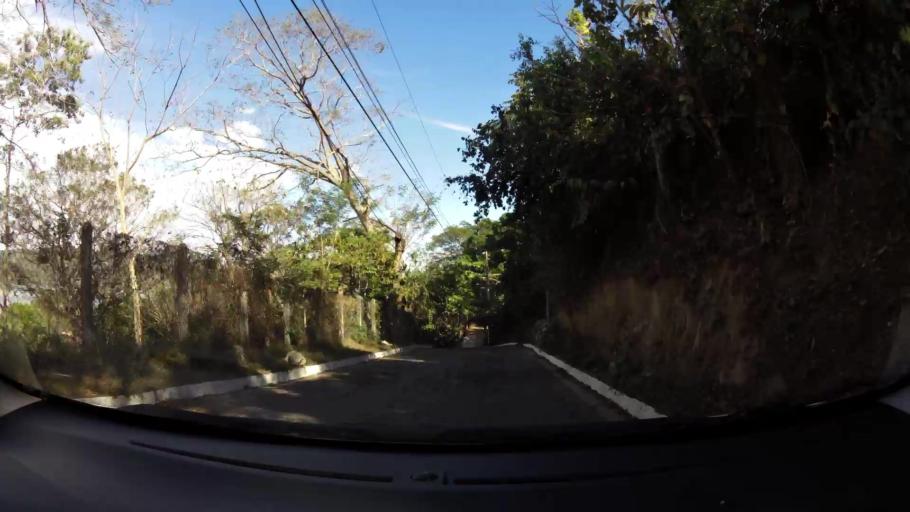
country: SV
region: Cuscatlan
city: Suchitoto
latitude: 13.9451
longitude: -89.0172
